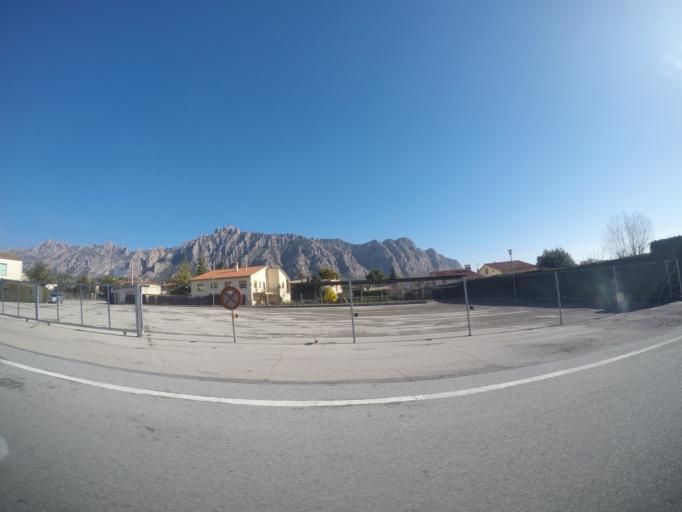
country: ES
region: Catalonia
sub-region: Provincia de Barcelona
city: Collbato
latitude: 41.5644
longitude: 1.8125
